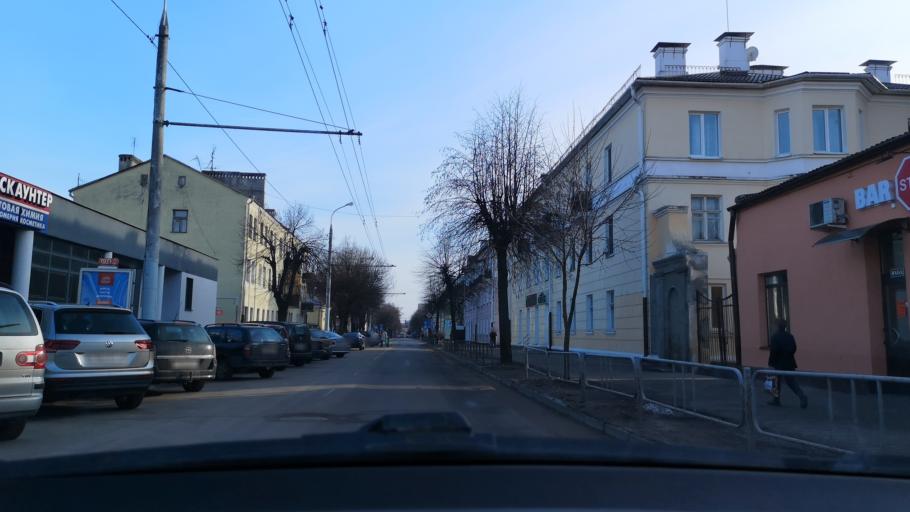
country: BY
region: Brest
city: Brest
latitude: 52.0980
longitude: 23.6853
